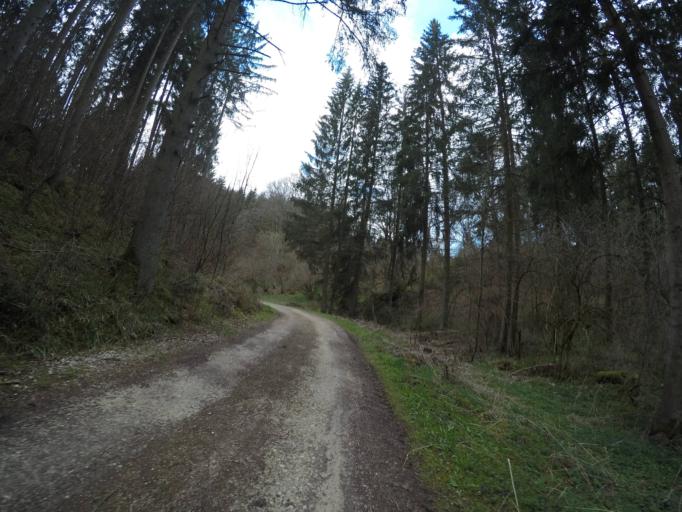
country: DE
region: Baden-Wuerttemberg
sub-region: Tuebingen Region
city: Nellingen
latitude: 48.5024
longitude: 9.7990
